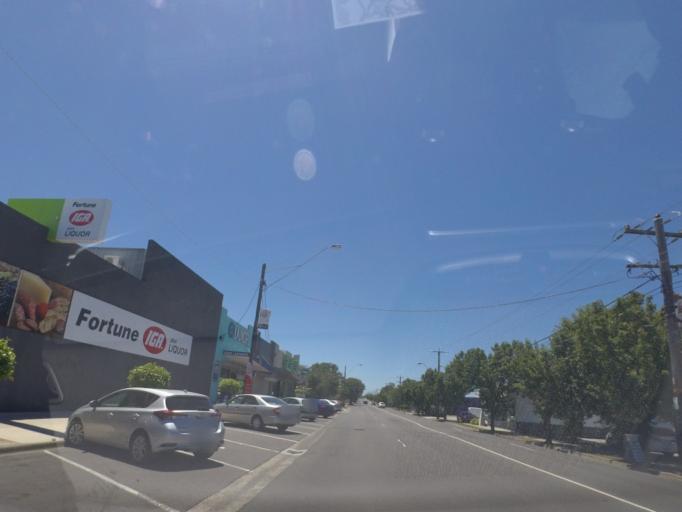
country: AU
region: Victoria
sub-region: Whittlesea
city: Thomastown
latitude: -37.6780
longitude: 145.0142
